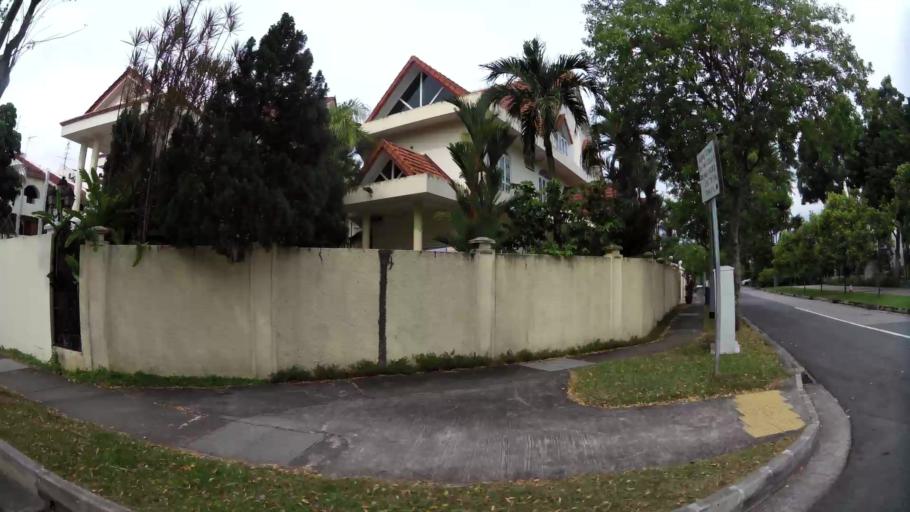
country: SG
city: Singapore
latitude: 1.3222
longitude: 103.7959
